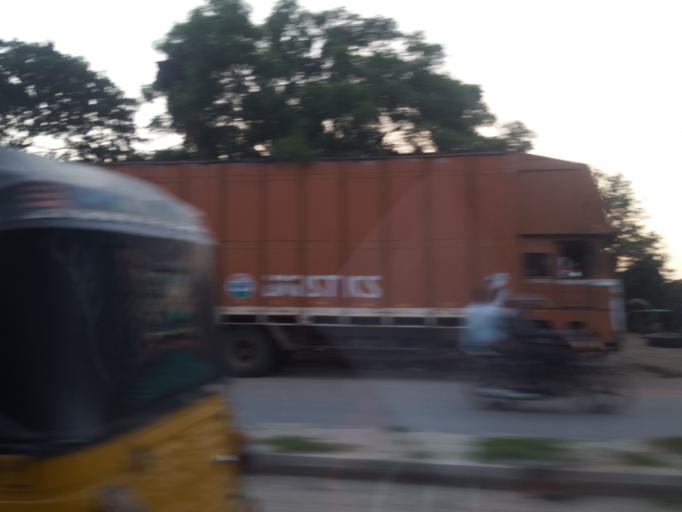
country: IN
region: Telangana
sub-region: Medak
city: Serilingampalle
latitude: 17.5371
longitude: 78.3584
